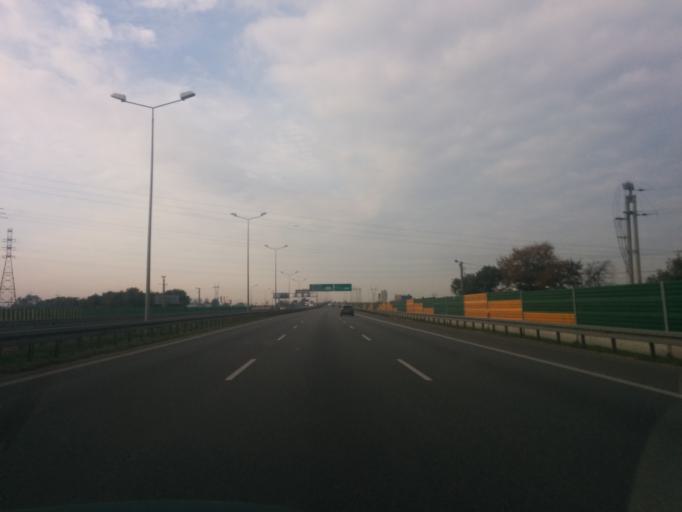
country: PL
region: Masovian Voivodeship
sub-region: Warszawa
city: Ursus
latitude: 52.2216
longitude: 20.8695
